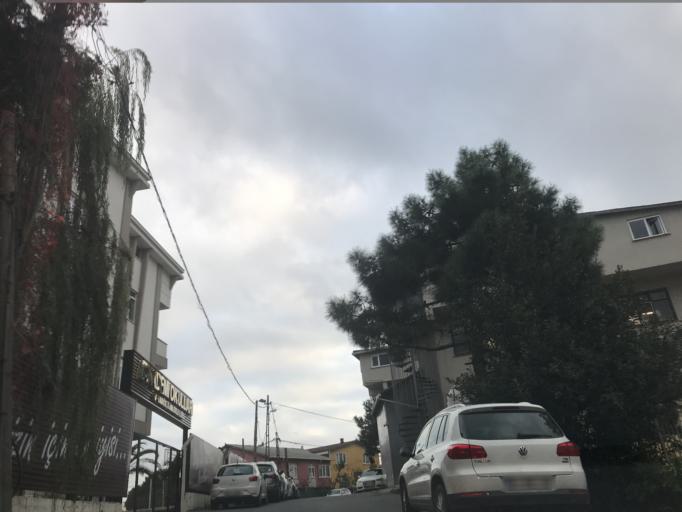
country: TR
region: Istanbul
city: Sisli
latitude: 41.1286
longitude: 29.0437
